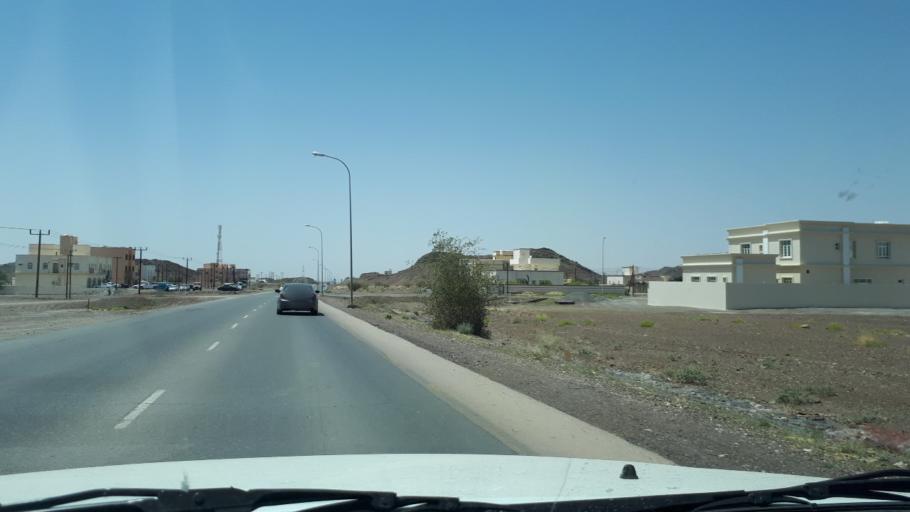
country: OM
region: Muhafazat ad Dakhiliyah
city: Bahla'
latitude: 22.9445
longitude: 57.2596
